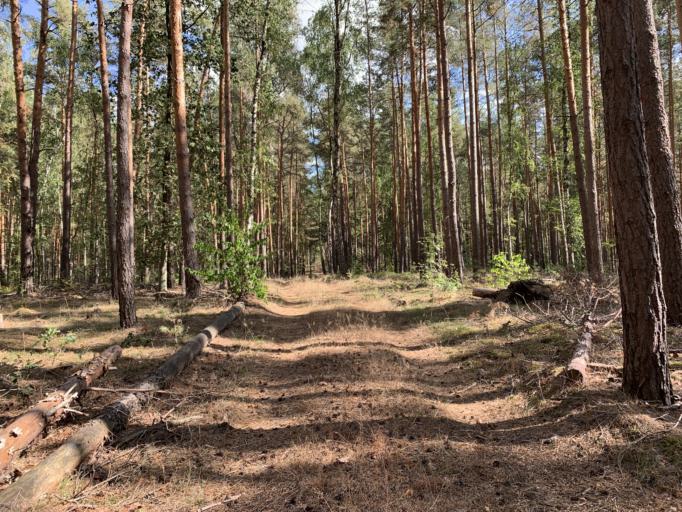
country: DE
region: Brandenburg
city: Michendorf
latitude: 52.3071
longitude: 12.9744
